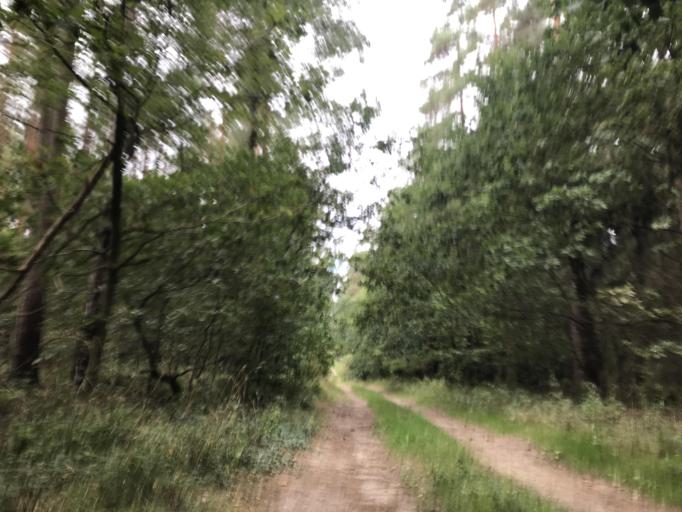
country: DE
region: Lower Saxony
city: Barendorf
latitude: 53.2448
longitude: 10.5351
